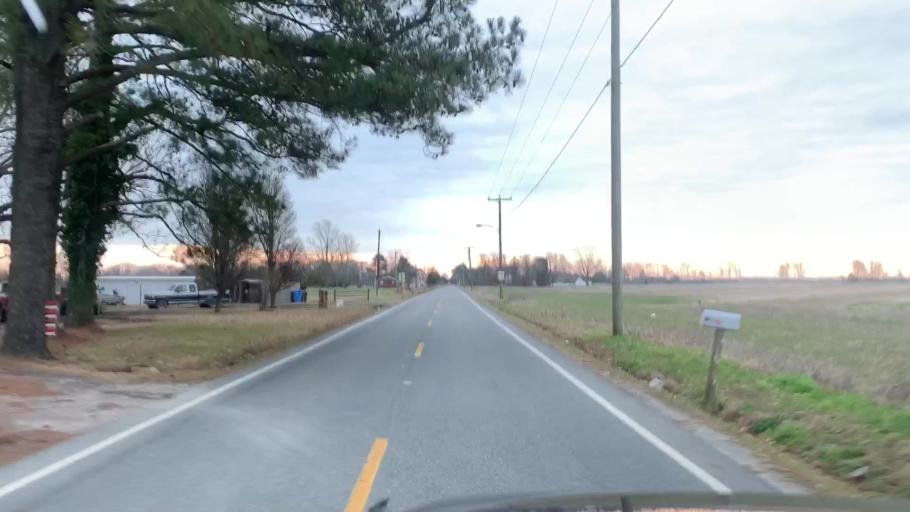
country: US
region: North Carolina
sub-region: Currituck County
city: Moyock
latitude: 36.6280
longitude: -76.1687
